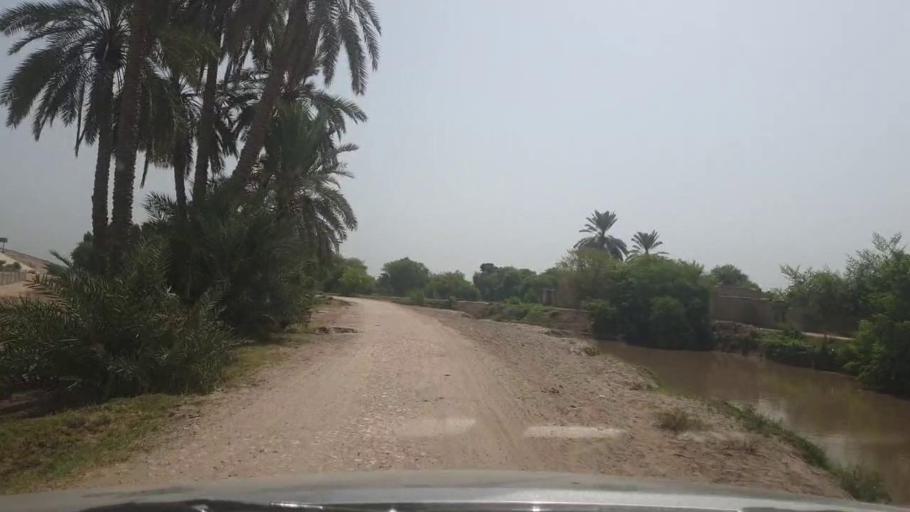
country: PK
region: Sindh
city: Pano Aqil
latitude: 27.9032
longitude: 69.1483
